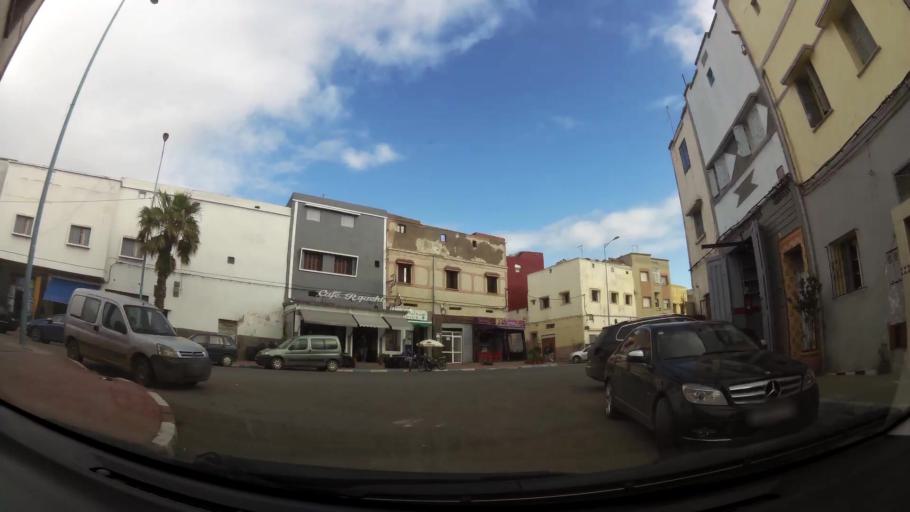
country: MA
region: Doukkala-Abda
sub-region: El-Jadida
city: El Jadida
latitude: 33.2586
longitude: -8.5146
